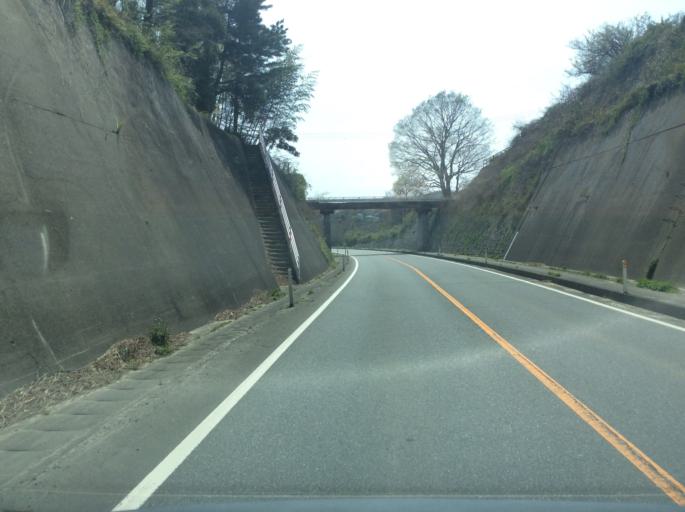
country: JP
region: Fukushima
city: Iwaki
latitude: 37.2113
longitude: 140.9940
